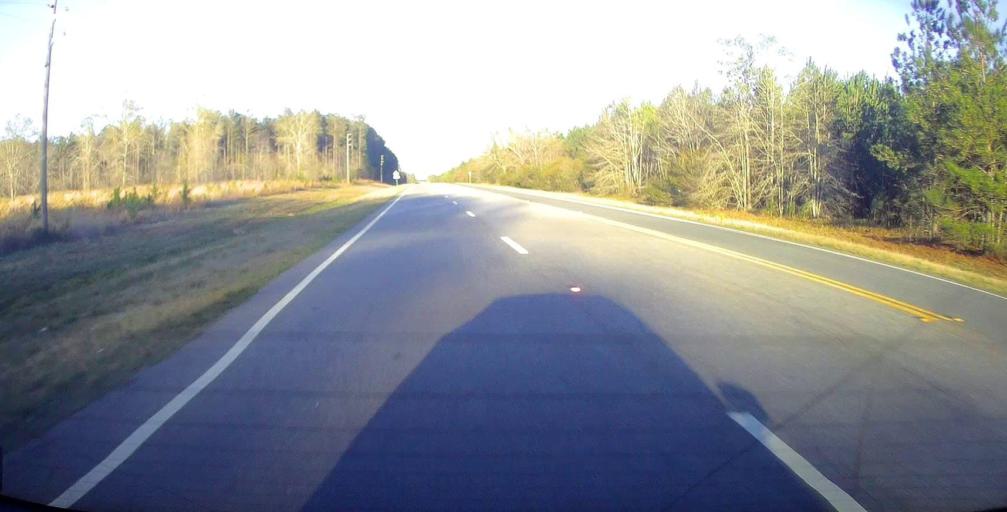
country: US
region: Georgia
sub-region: Wilcox County
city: Rochelle
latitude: 31.9626
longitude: -83.3965
